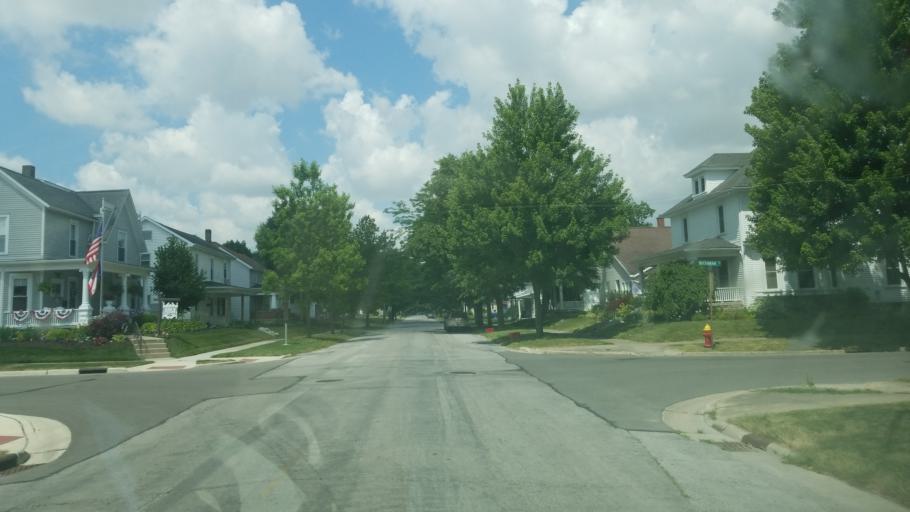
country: US
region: Ohio
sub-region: Auglaize County
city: Wapakoneta
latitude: 40.5671
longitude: -84.2017
